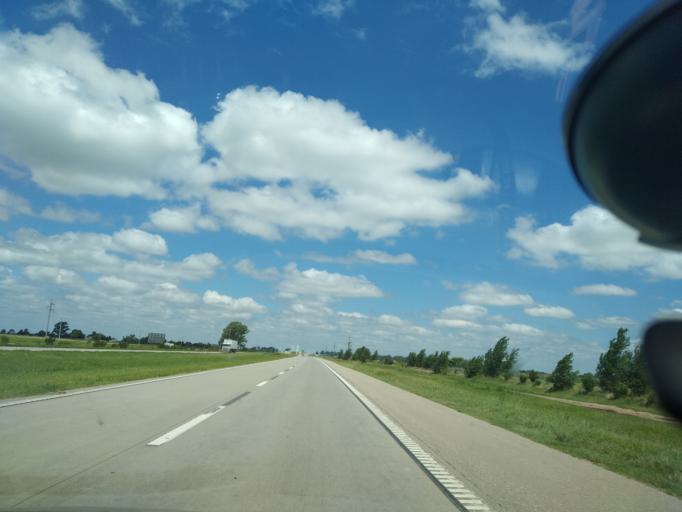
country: AR
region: Cordoba
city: Villa Maria
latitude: -32.3497
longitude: -63.2465
